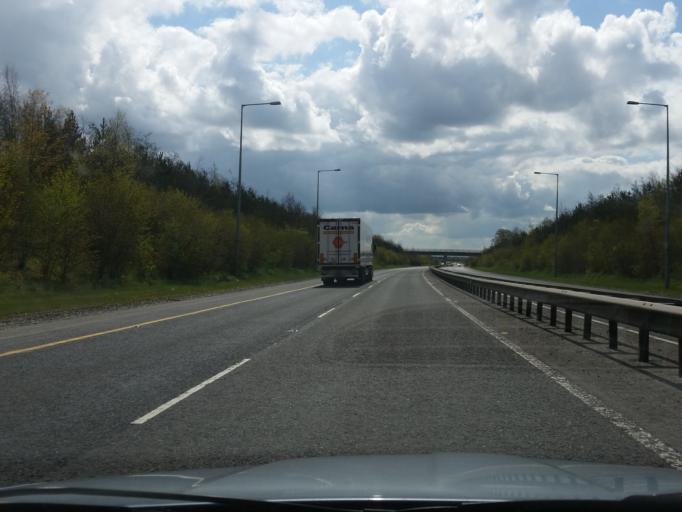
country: IE
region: Leinster
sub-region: An Mhi
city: Ashbourne
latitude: 53.5204
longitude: -6.4192
